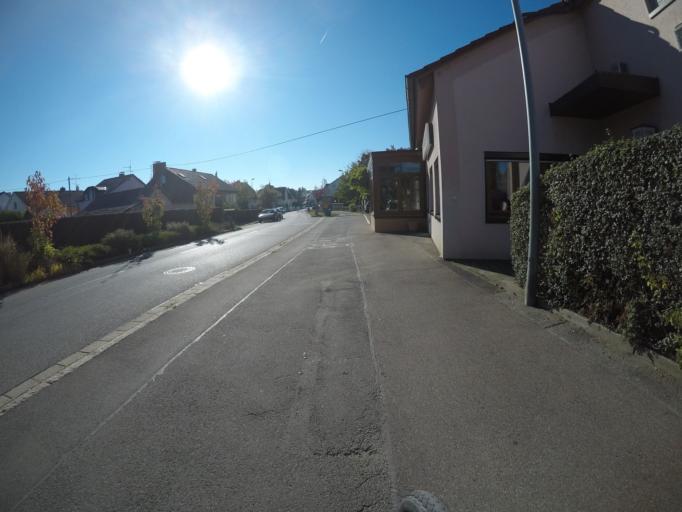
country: DE
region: Baden-Wuerttemberg
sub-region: Regierungsbezirk Stuttgart
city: Filderstadt
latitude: 48.6596
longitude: 9.2180
